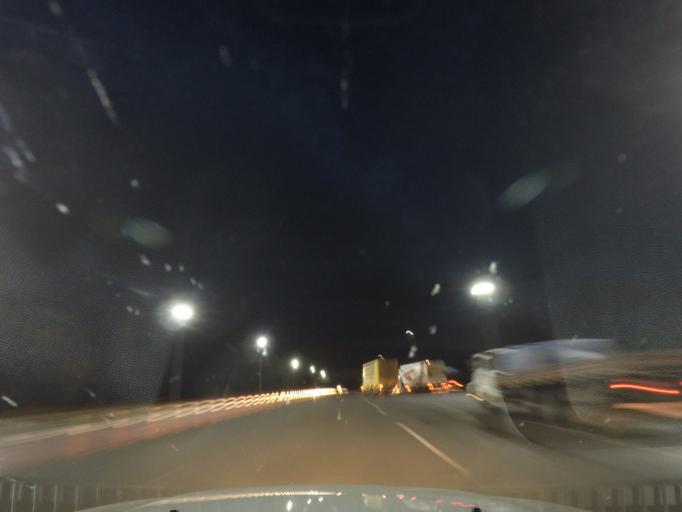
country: BR
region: Minas Gerais
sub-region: Uberlandia
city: Uberlandia
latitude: -19.1799
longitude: -48.1576
